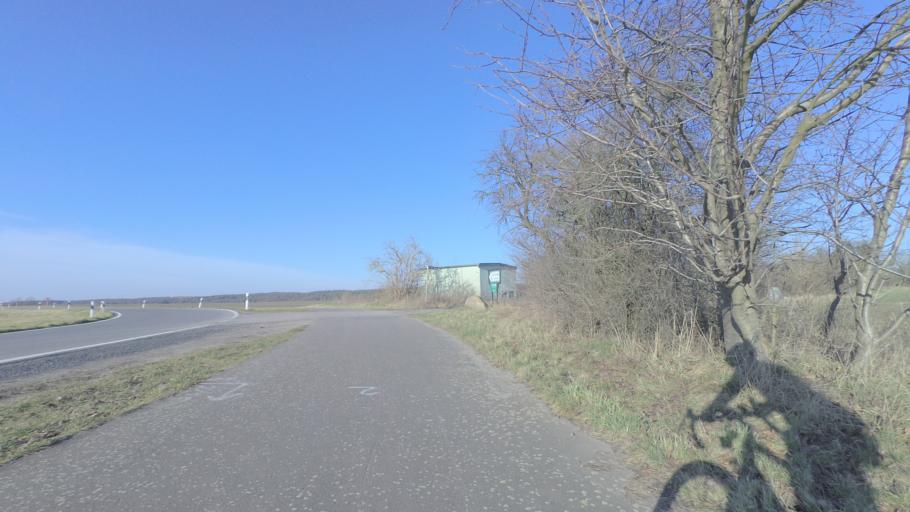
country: DE
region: Brandenburg
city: Ihlow
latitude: 51.9913
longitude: 13.3567
